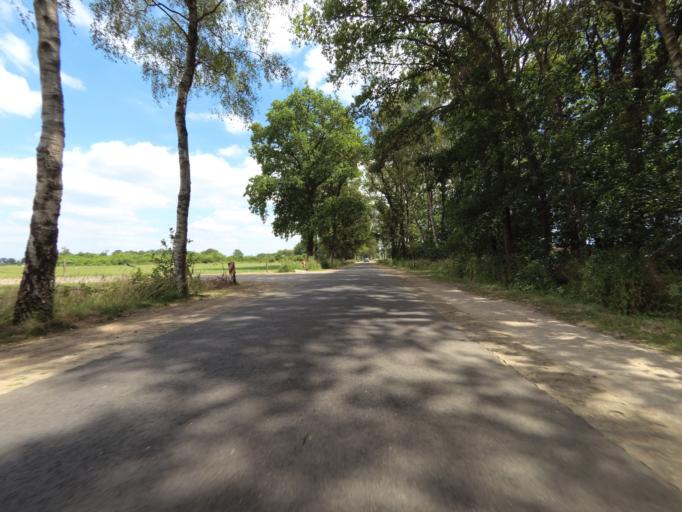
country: NL
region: Overijssel
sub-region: Gemeente Raalte
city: Raalte
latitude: 52.3148
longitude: 6.3050
